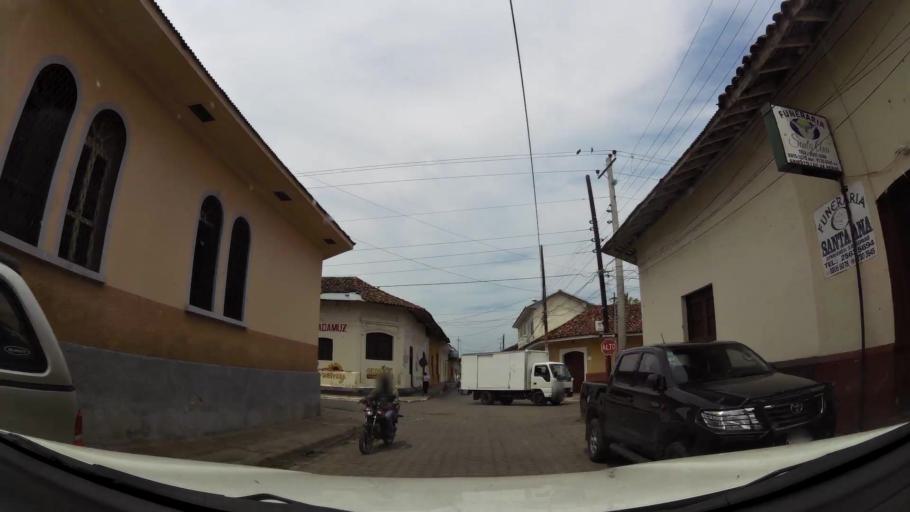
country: NI
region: Rivas
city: Rivas
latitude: 11.4369
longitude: -85.8311
